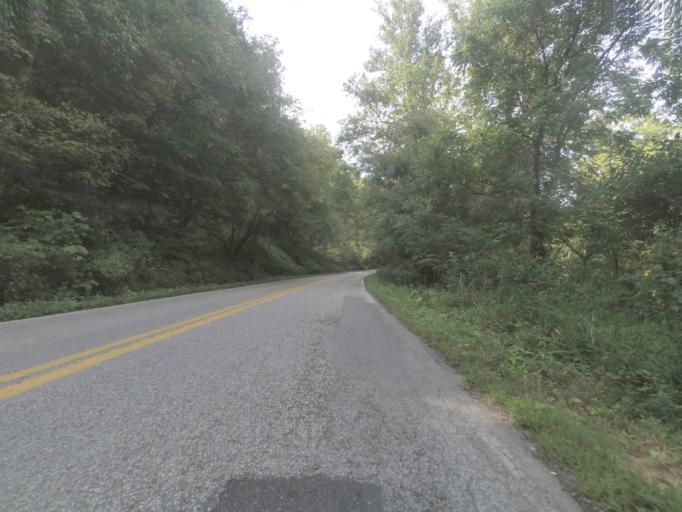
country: US
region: West Virginia
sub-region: Wayne County
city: Ceredo
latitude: 38.3719
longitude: -82.5523
